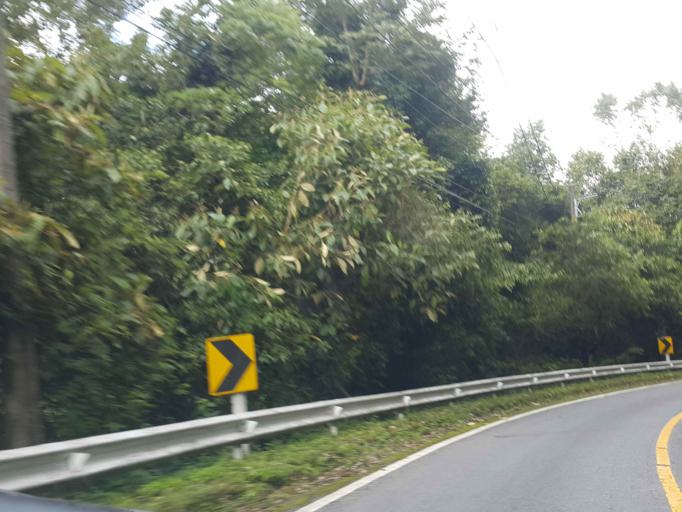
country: TH
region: Chiang Mai
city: Mae Chaem
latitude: 18.5464
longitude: 98.4869
